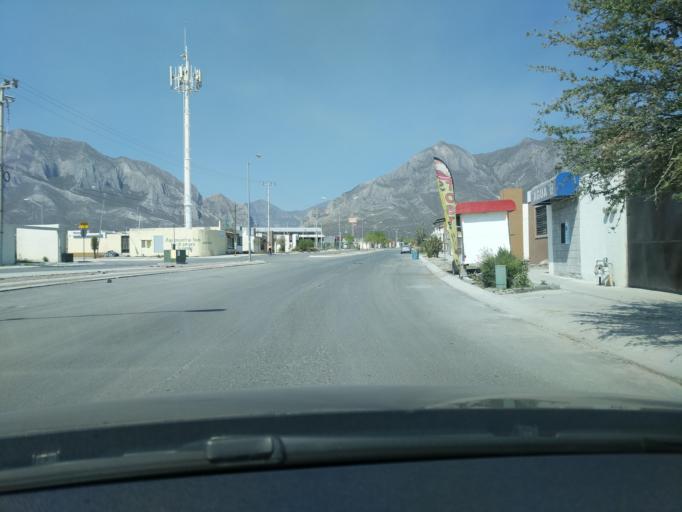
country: MX
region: Nuevo Leon
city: Garcia
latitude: 25.8166
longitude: -100.5398
